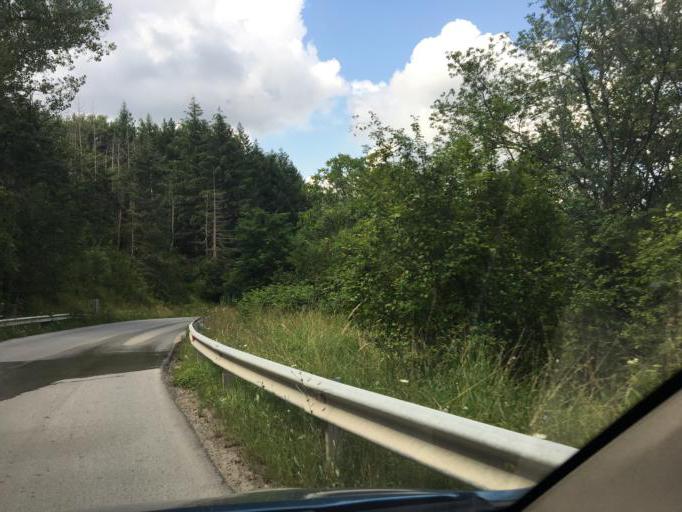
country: BG
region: Sofia-Capital
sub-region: Stolichna Obshtina
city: Sofia
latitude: 42.5943
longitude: 23.3648
